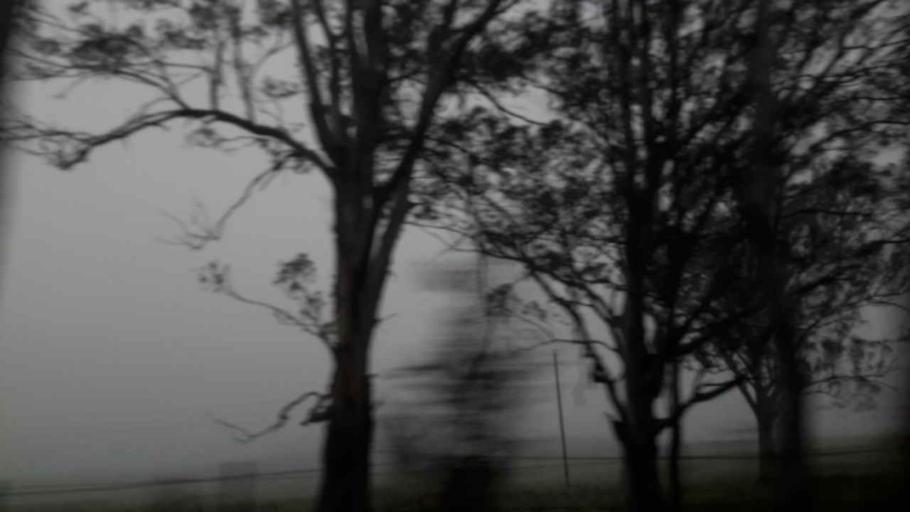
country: AU
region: New South Wales
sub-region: Wollondilly
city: Douglas Park
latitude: -34.2100
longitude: 150.7199
